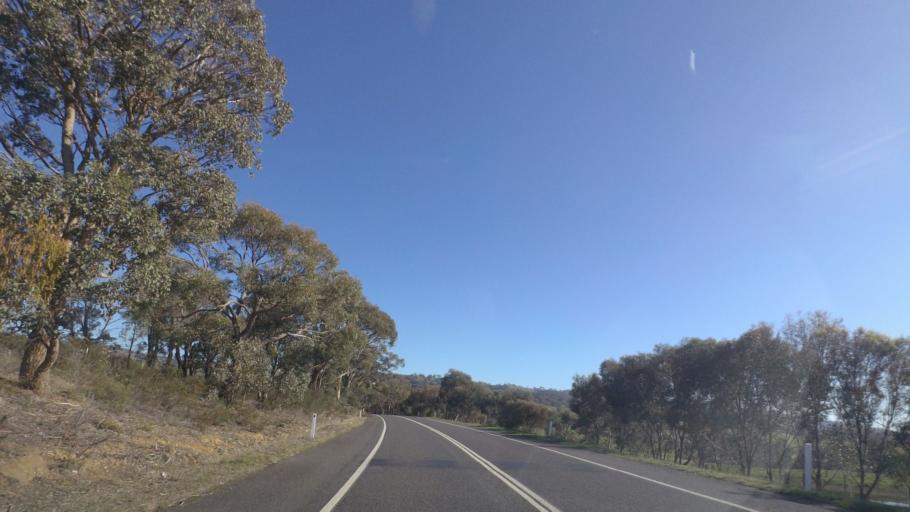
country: AU
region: Victoria
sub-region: Greater Bendigo
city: Kennington
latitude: -36.9107
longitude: 144.3215
